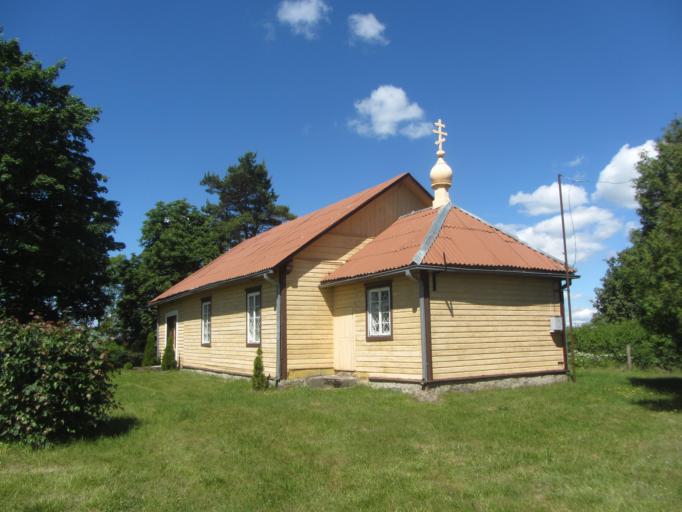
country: LT
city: Jieznas
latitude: 54.7578
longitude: 24.2316
